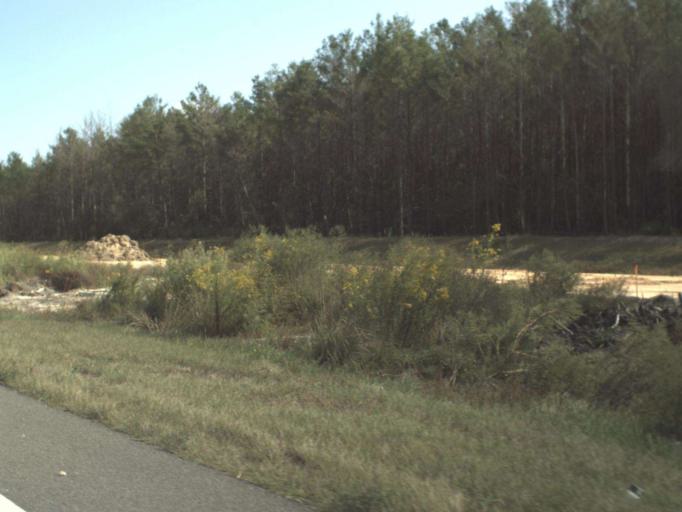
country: US
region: Florida
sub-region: Walton County
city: Freeport
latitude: 30.5065
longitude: -86.1149
